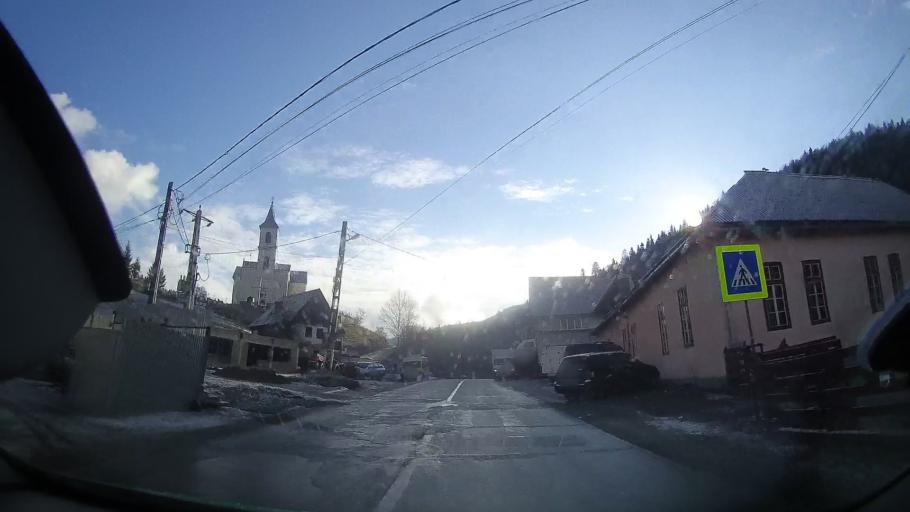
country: RO
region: Alba
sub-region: Comuna Vadu Motilor
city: Vadu Motilor
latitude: 46.3944
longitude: 22.9654
